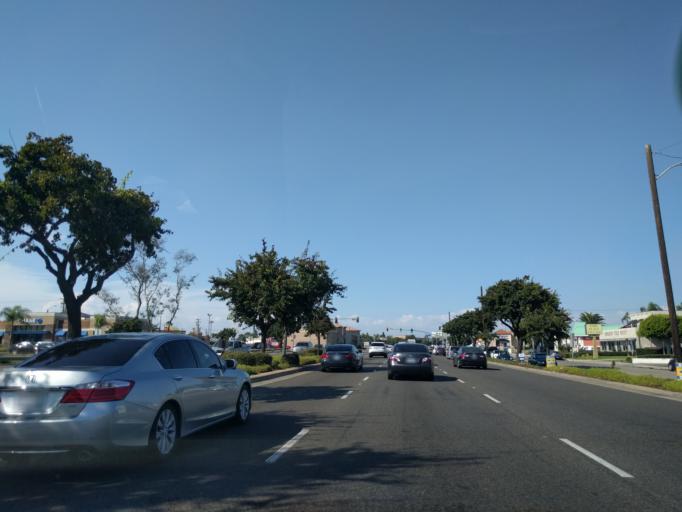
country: US
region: California
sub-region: Orange County
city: Costa Mesa
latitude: 33.6350
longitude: -117.9223
